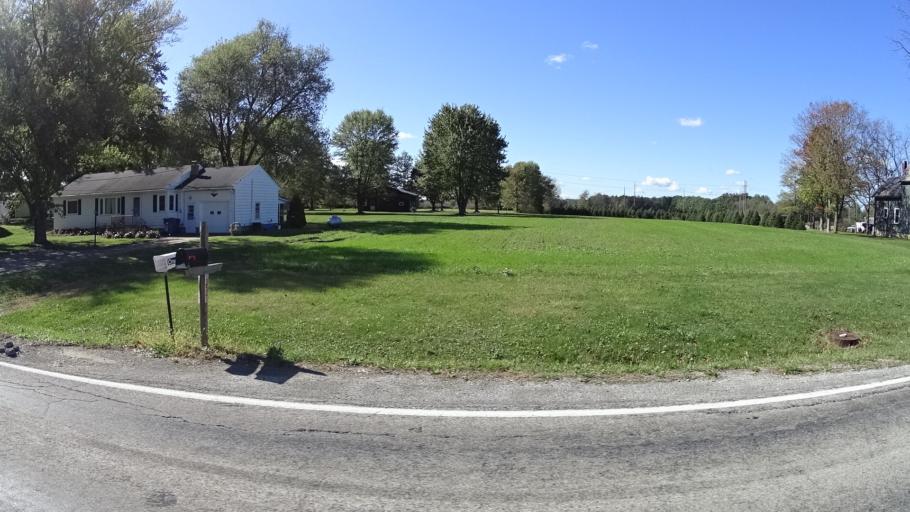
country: US
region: Ohio
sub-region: Lorain County
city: Grafton
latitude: 41.2900
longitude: -82.0833
